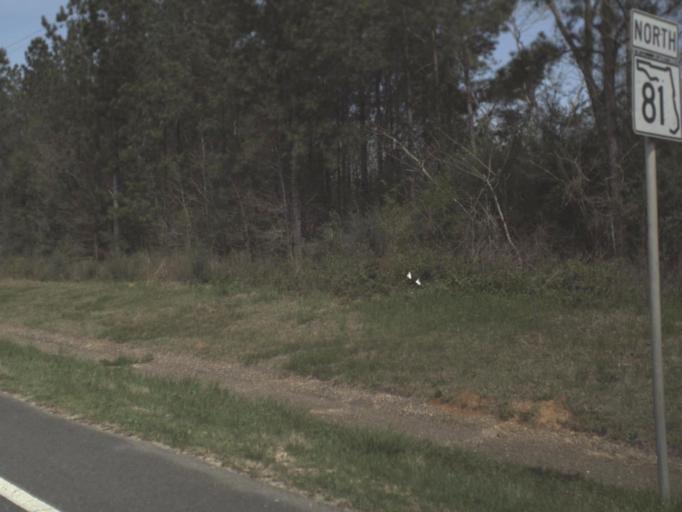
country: US
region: Alabama
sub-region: Geneva County
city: Geneva
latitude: 30.9157
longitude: -85.9600
